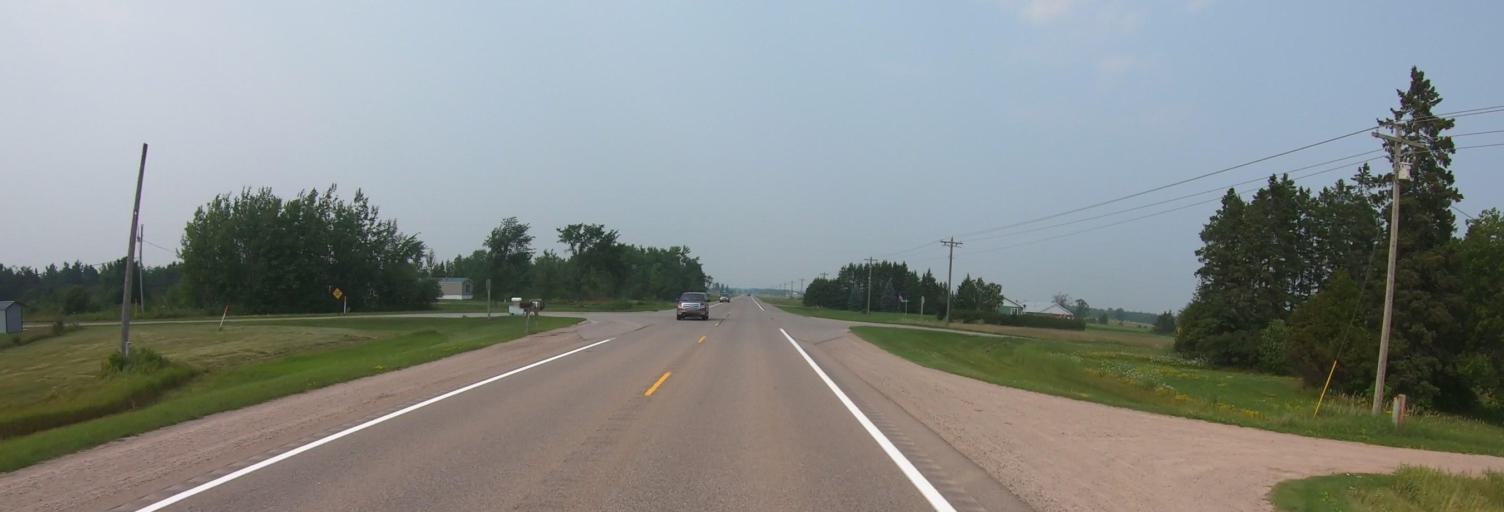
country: US
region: Michigan
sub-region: Chippewa County
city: Sault Ste. Marie
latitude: 46.3460
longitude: -84.3640
